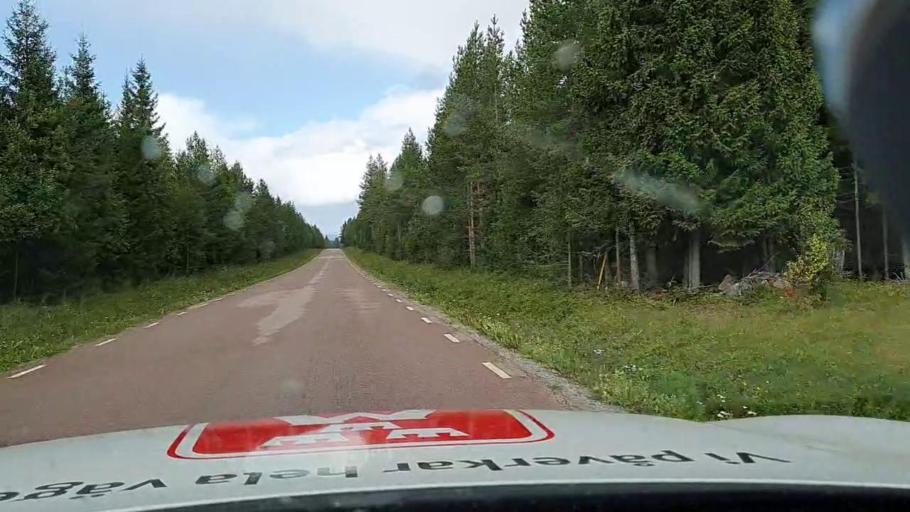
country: SE
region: Jaemtland
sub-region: Stroemsunds Kommun
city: Stroemsund
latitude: 63.8719
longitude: 15.3675
